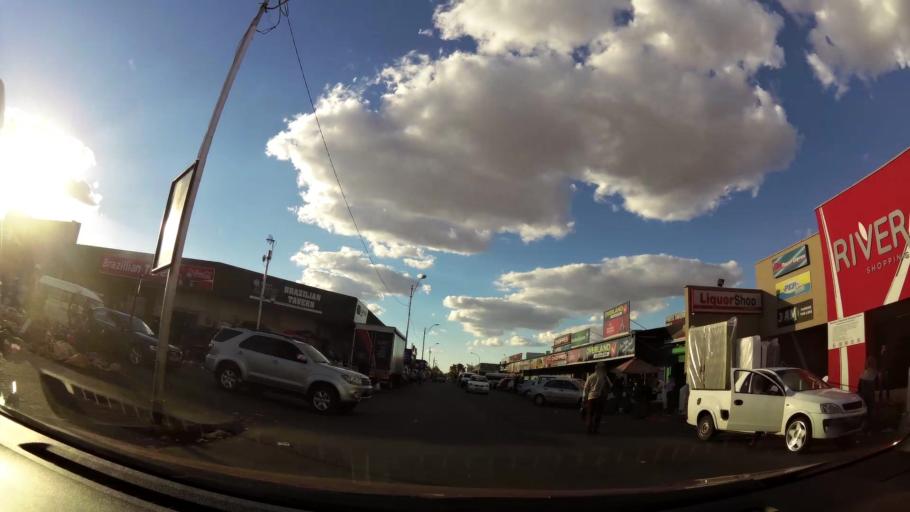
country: ZA
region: North-West
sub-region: Dr Kenneth Kaunda District Municipality
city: Potchefstroom
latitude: -26.7123
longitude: 27.1013
